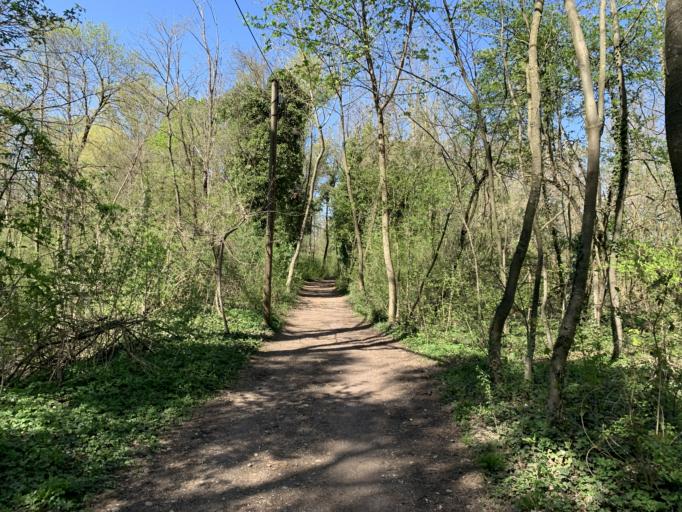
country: DE
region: Bavaria
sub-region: Swabia
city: Gersthofen
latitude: 48.4331
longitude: 10.8921
